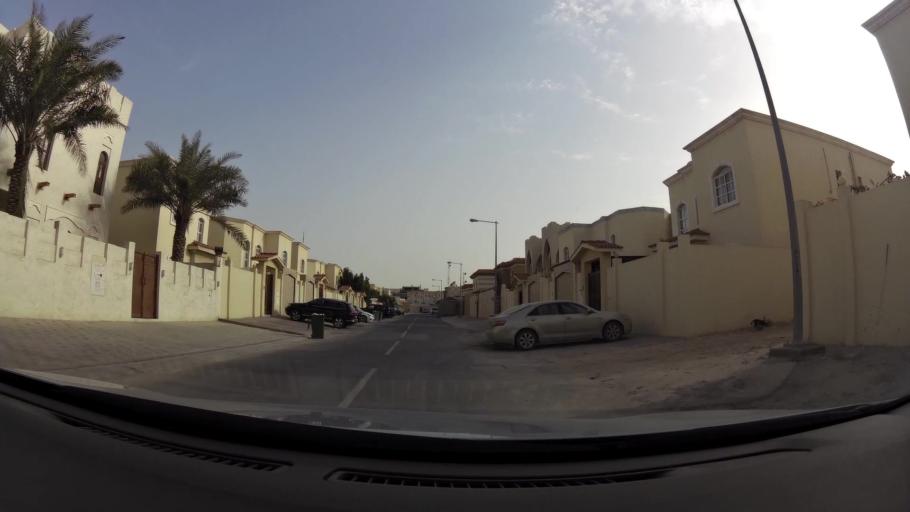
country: QA
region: Baladiyat ad Dawhah
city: Doha
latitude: 25.3207
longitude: 51.5006
